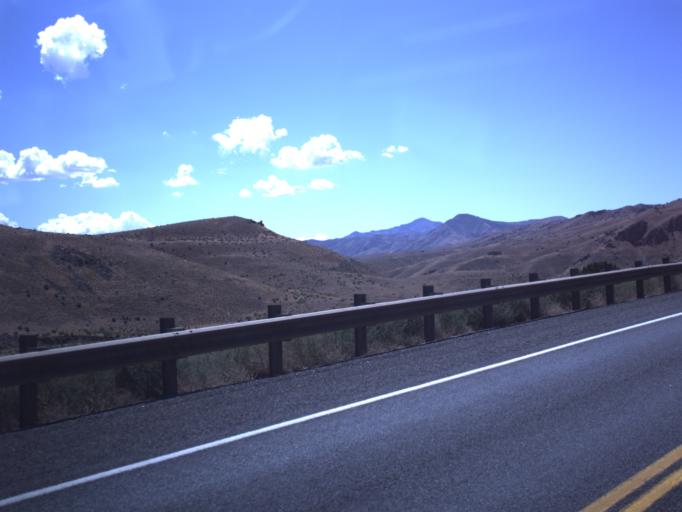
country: US
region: Utah
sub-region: Juab County
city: Nephi
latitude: 39.5965
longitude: -112.1473
